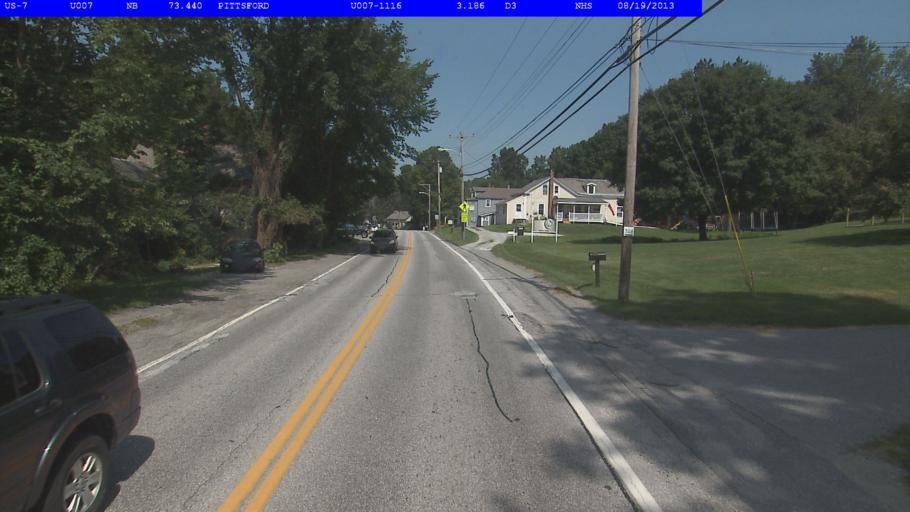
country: US
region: Vermont
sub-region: Rutland County
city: Rutland
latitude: 43.7048
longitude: -73.0136
